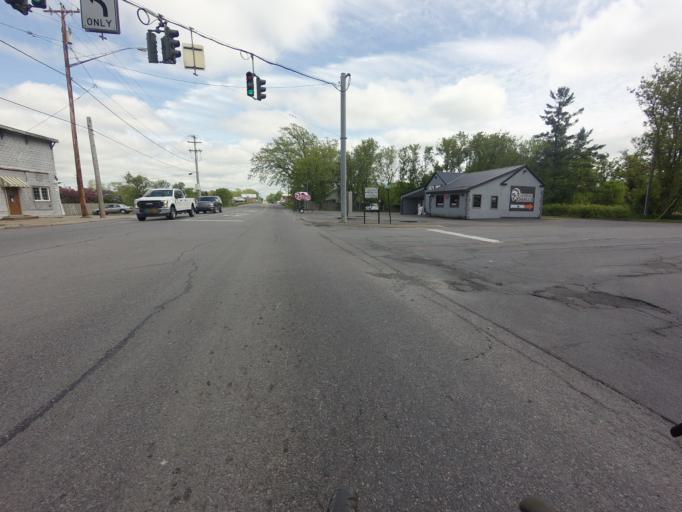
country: CA
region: Ontario
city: Cornwall
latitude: 44.9738
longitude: -74.6676
